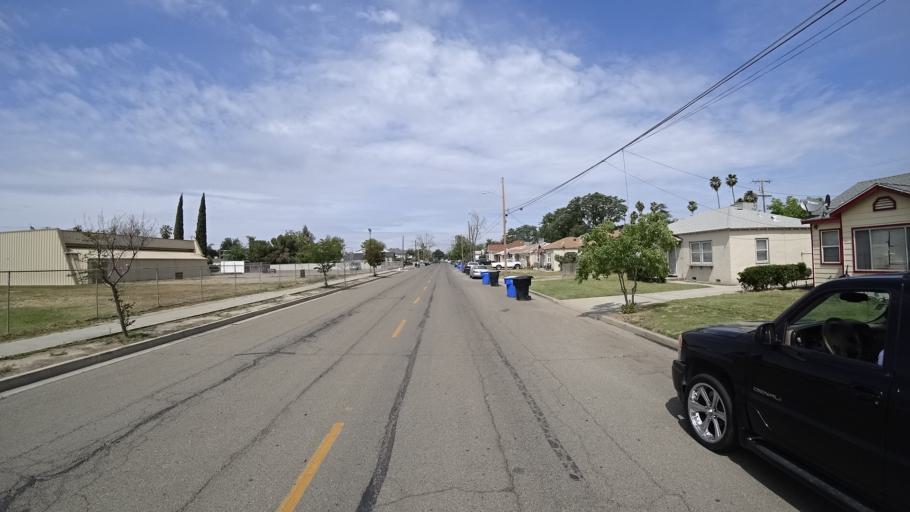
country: US
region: California
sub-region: Kings County
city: Hanford
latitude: 36.3331
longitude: -119.6405
